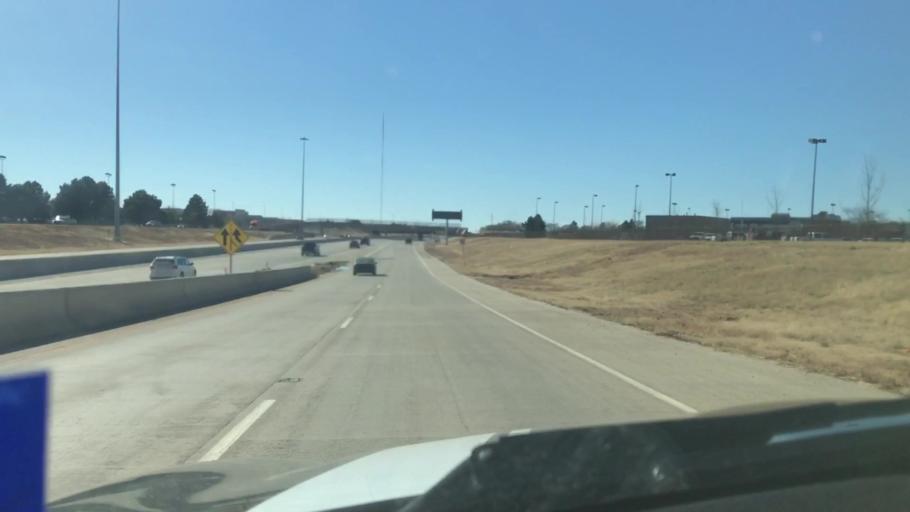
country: US
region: Texas
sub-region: Lubbock County
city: Lubbock
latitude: 33.5916
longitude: -101.8786
